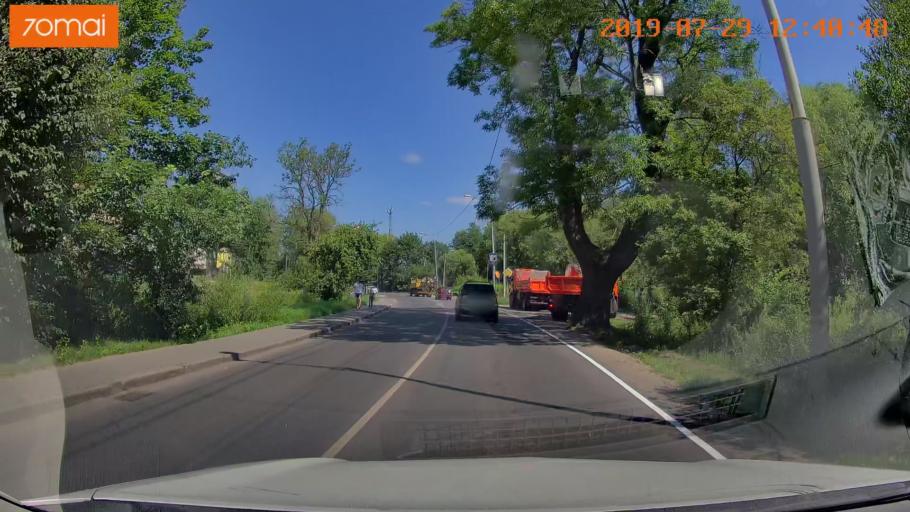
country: RU
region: Kaliningrad
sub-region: Gorod Kaliningrad
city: Kaliningrad
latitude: 54.6693
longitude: 20.5452
